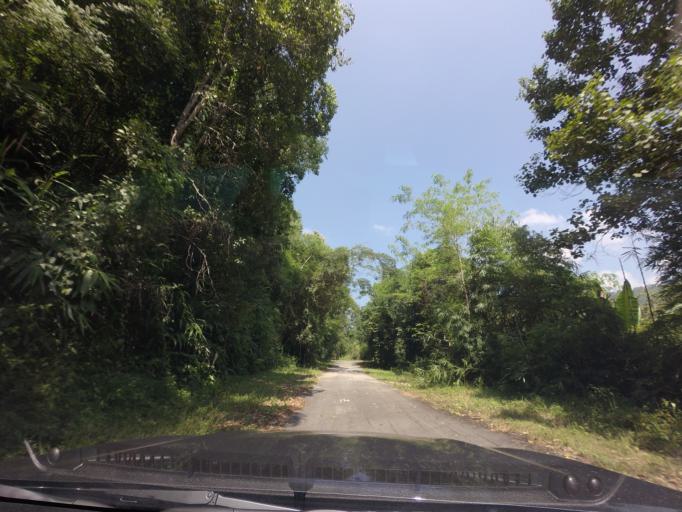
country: TH
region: Loei
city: Na Haeo
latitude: 17.5692
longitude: 100.9775
